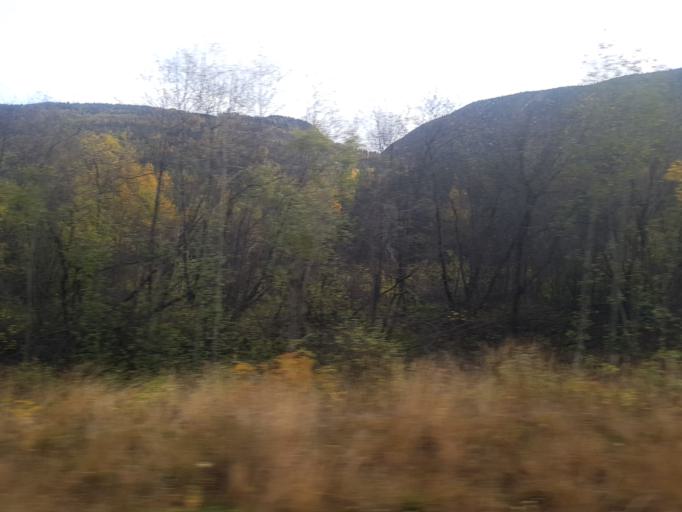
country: NO
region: Oppland
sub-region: Sel
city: Otta
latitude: 61.8066
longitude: 9.5347
